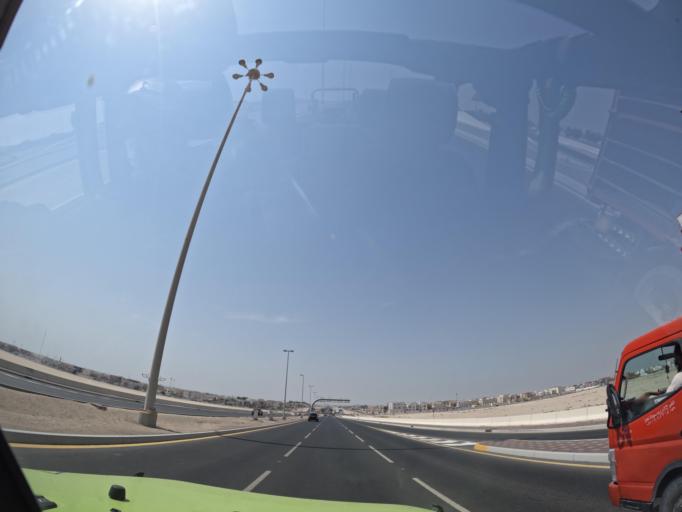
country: AE
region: Abu Dhabi
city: Abu Dhabi
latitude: 24.3414
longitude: 54.6351
